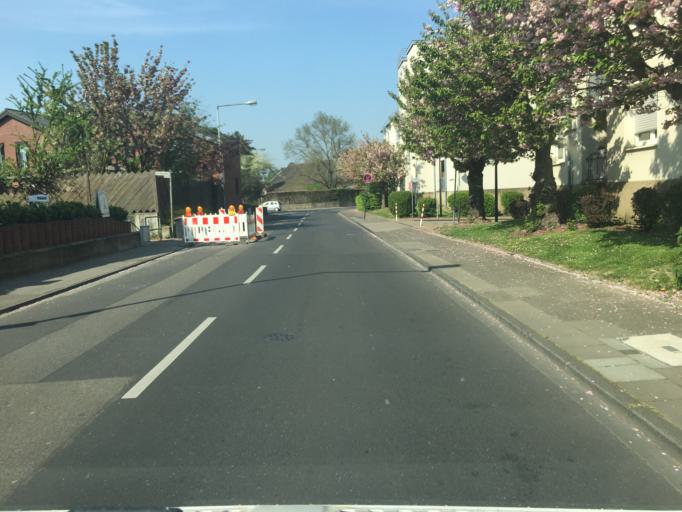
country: DE
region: North Rhine-Westphalia
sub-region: Regierungsbezirk Koln
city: Frechen
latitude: 50.9431
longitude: 6.8293
